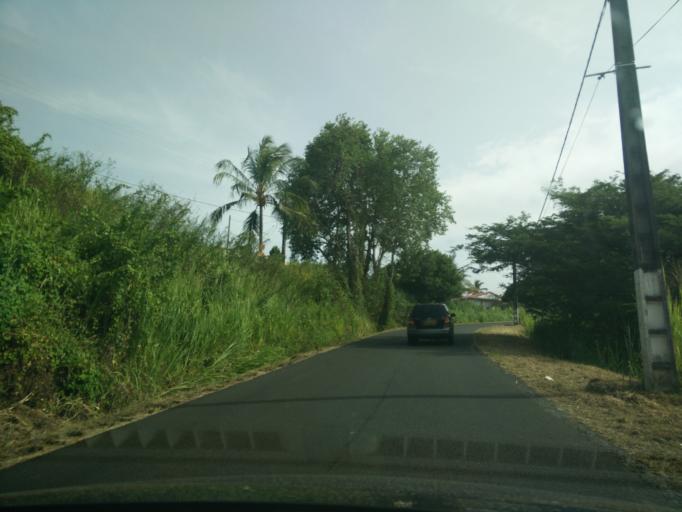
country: GP
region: Guadeloupe
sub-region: Guadeloupe
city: Petit-Bourg
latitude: 16.1335
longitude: -61.5825
